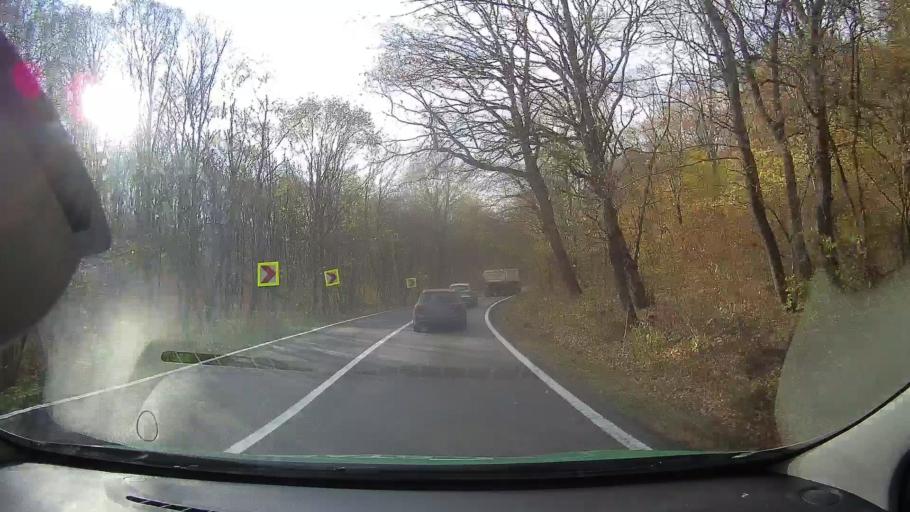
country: RO
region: Tulcea
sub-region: Comuna Ciucurova
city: Ciucurova
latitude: 44.9243
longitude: 28.4372
